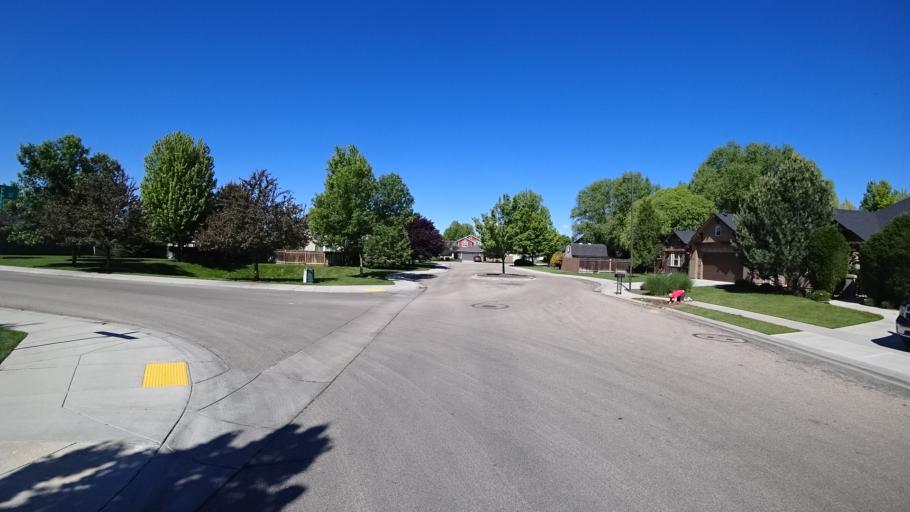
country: US
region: Idaho
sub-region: Ada County
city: Meridian
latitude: 43.6378
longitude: -116.3870
